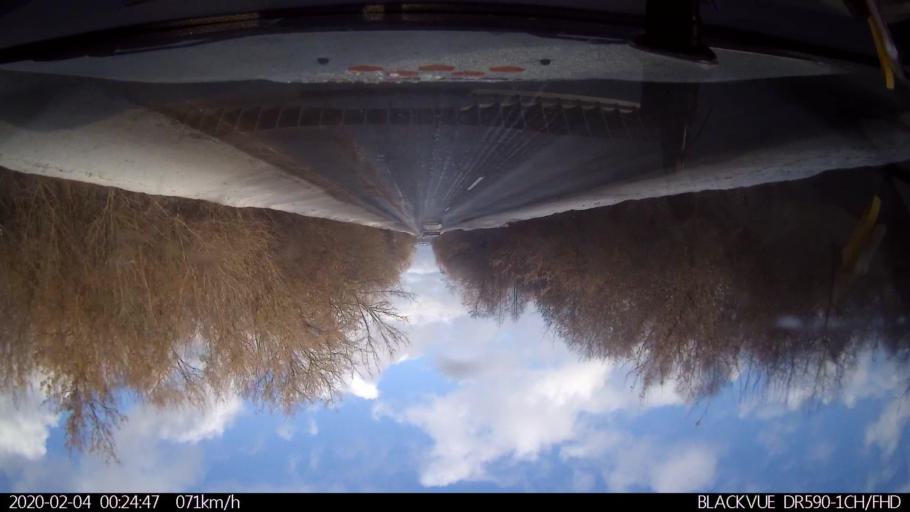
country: RU
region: Nizjnij Novgorod
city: Kstovo
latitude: 55.9988
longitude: 44.2117
